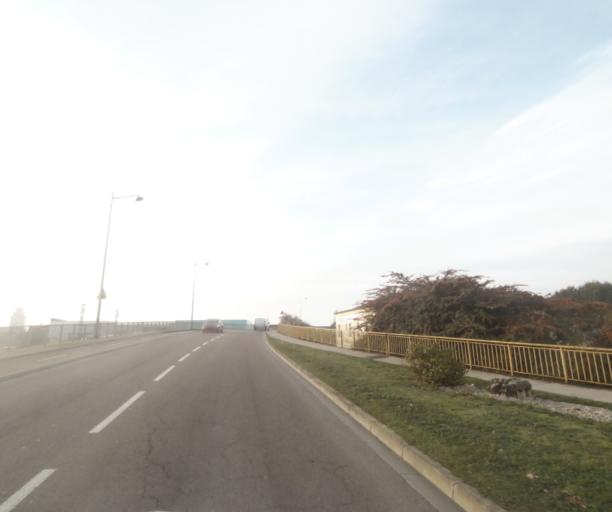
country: FR
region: Champagne-Ardenne
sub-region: Departement de la Haute-Marne
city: Saint-Dizier
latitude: 48.6425
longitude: 4.9513
